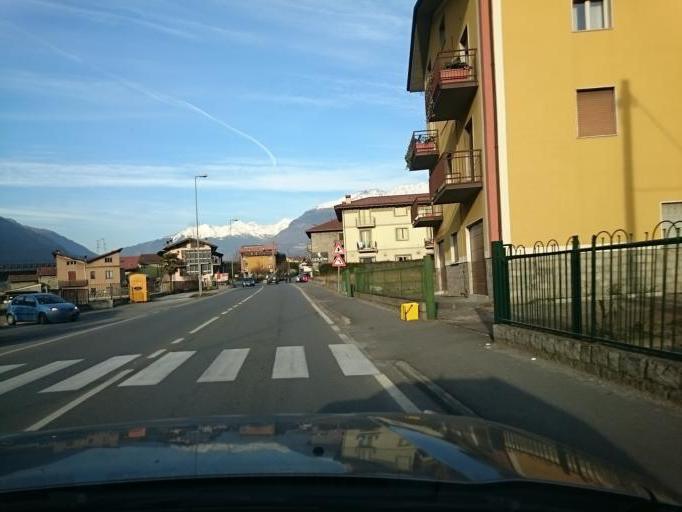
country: IT
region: Lombardy
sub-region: Provincia di Brescia
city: Breno
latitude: 45.9657
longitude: 10.3167
